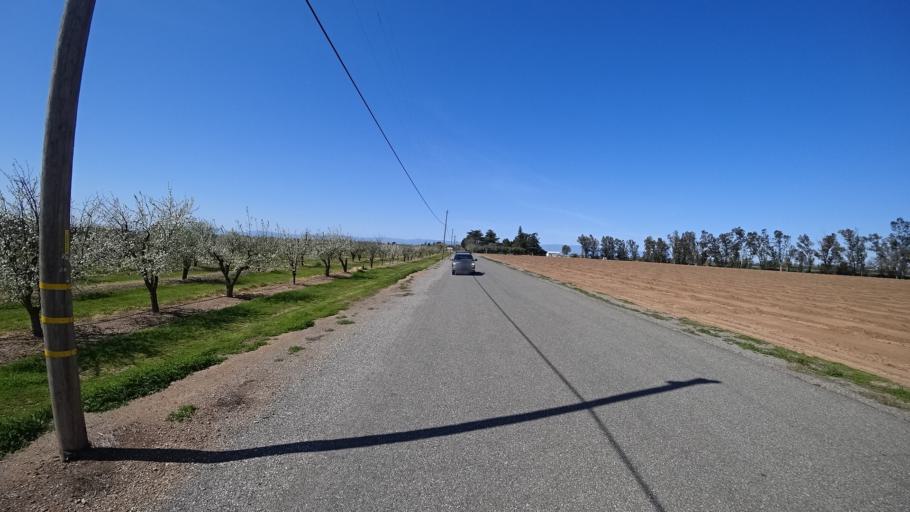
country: US
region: California
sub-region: Glenn County
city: Hamilton City
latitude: 39.7969
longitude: -122.0729
